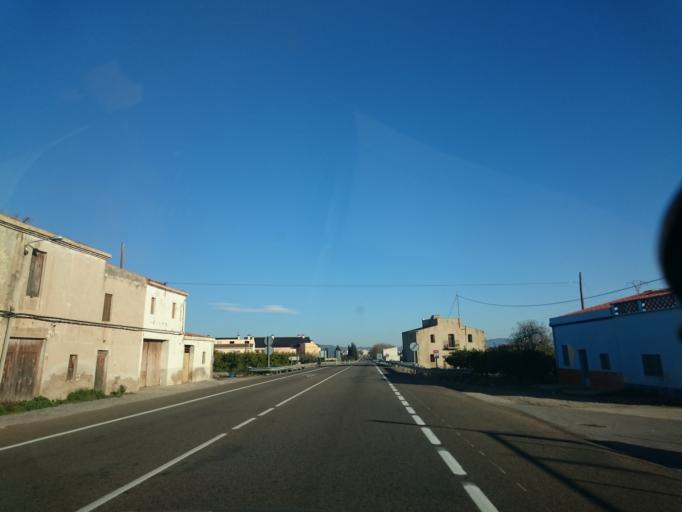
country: ES
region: Valencia
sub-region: Provincia de Castello
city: Orpesa/Oropesa del Mar
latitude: 40.1401
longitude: 0.1520
